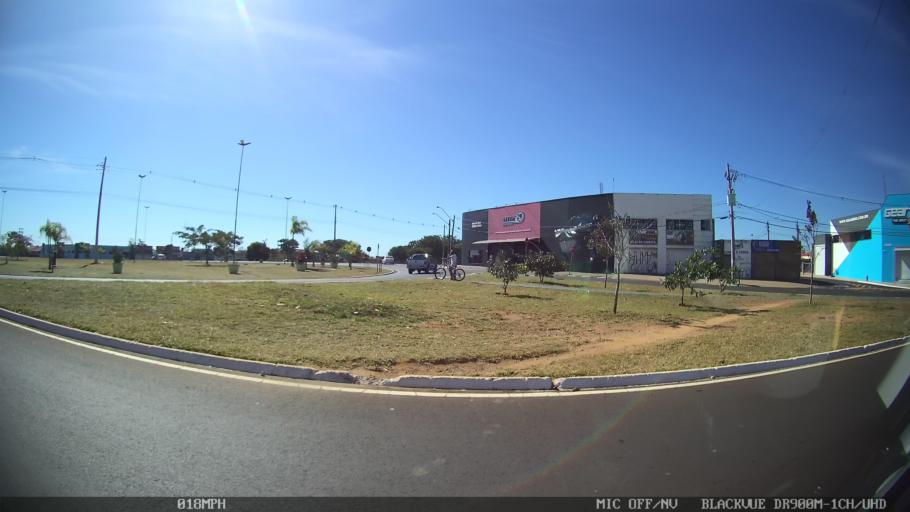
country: BR
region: Sao Paulo
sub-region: Franca
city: Franca
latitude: -20.5414
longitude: -47.3599
